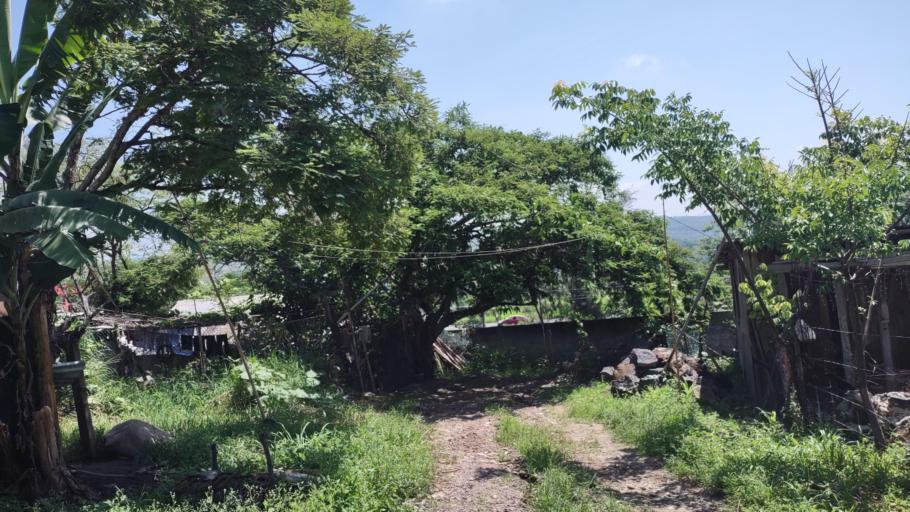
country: MX
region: Veracruz
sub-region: Emiliano Zapata
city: Dos Rios
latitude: 19.4914
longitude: -96.8159
